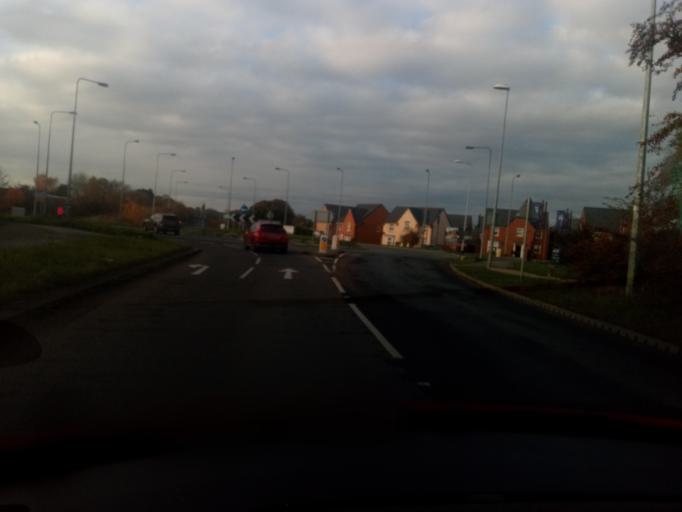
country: GB
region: England
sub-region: City and Borough of Leeds
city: Wetherby
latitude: 53.9389
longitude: -1.3787
